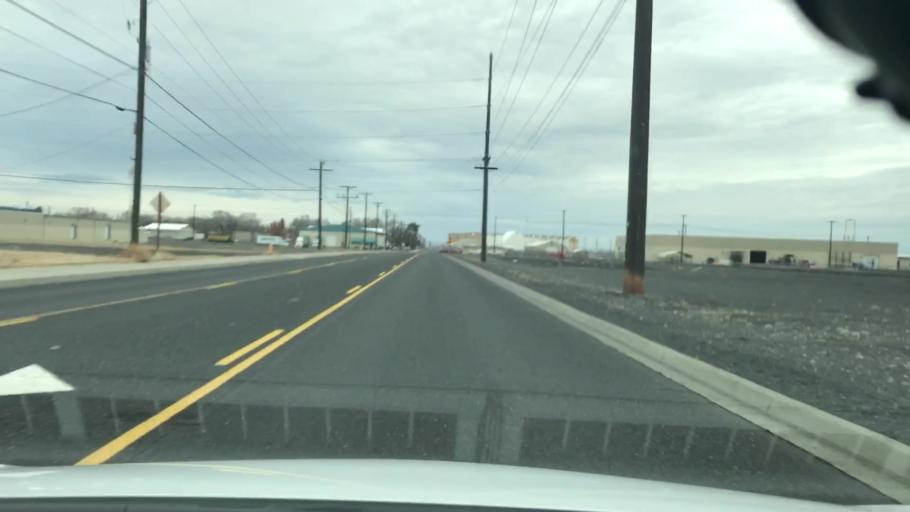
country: US
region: Washington
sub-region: Grant County
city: Moses Lake North
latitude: 47.1794
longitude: -119.3165
